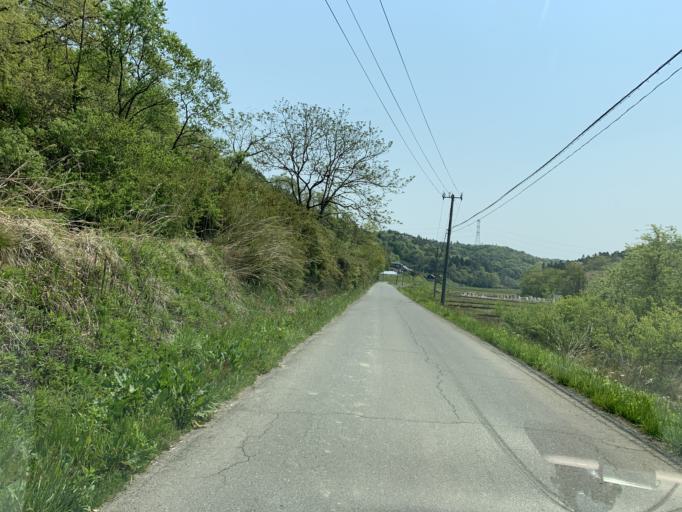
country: JP
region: Iwate
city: Ichinoseki
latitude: 38.8479
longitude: 141.0600
